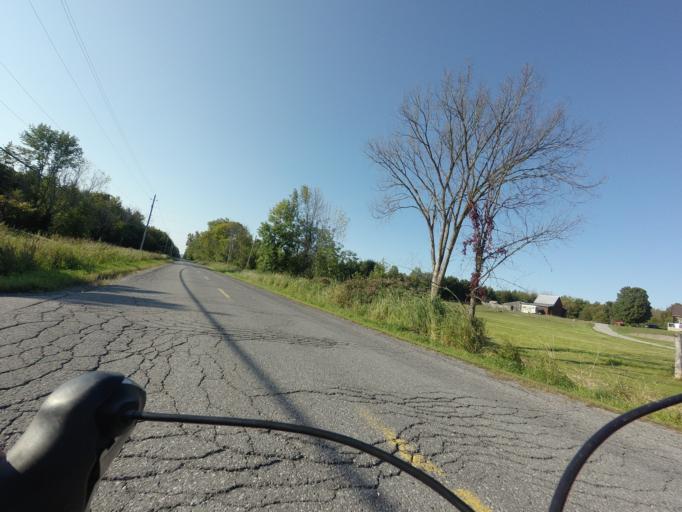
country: CA
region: Ontario
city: Bells Corners
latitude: 45.4686
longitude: -76.0303
